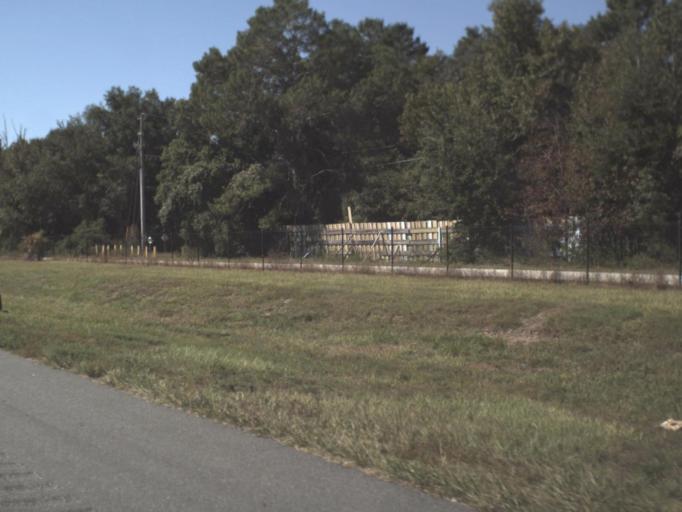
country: US
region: Florida
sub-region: Pasco County
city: Shady Hills
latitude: 28.3958
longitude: -82.5271
